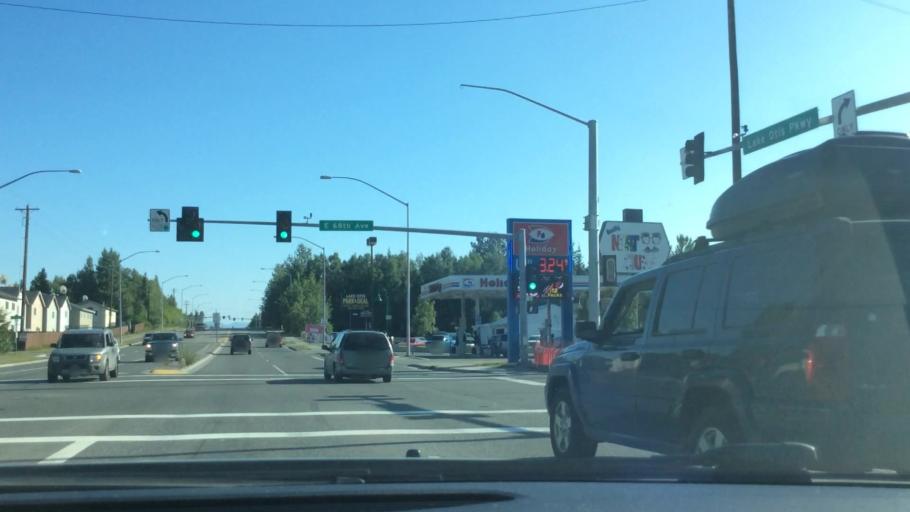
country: US
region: Alaska
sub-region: Anchorage Municipality
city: Anchorage
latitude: 61.1594
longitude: -149.8343
